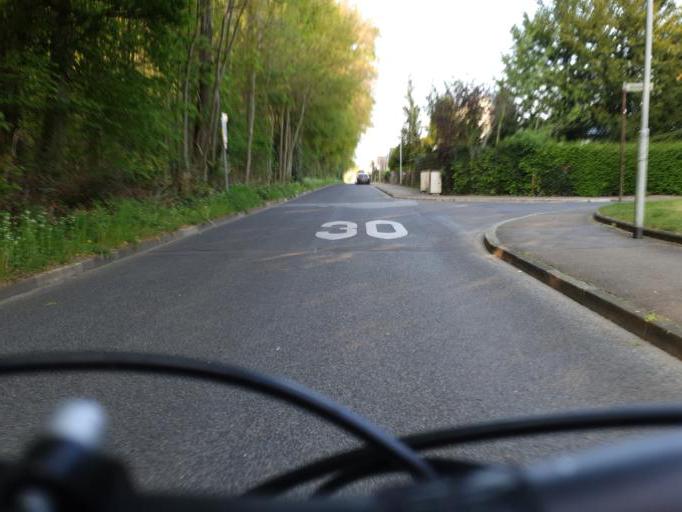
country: DE
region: North Rhine-Westphalia
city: Opladen
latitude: 51.0470
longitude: 7.0486
